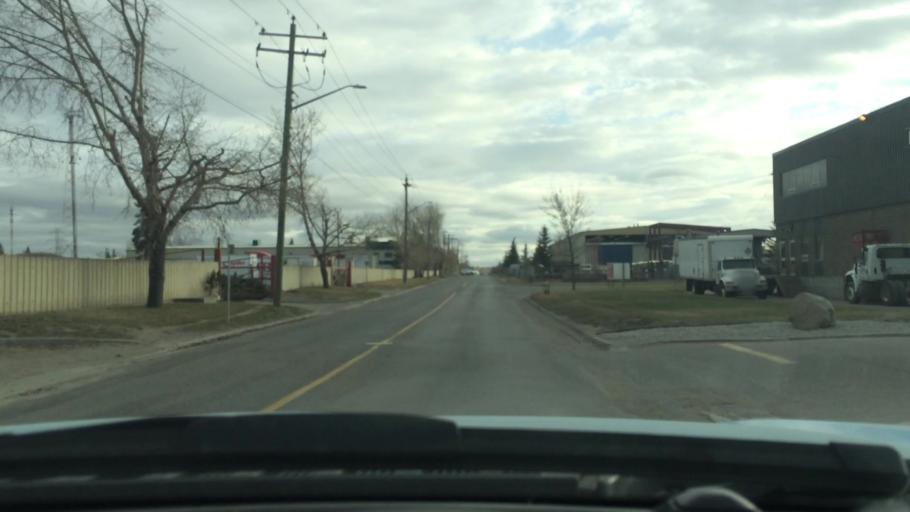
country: CA
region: Alberta
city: Calgary
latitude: 51.0037
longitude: -113.9655
